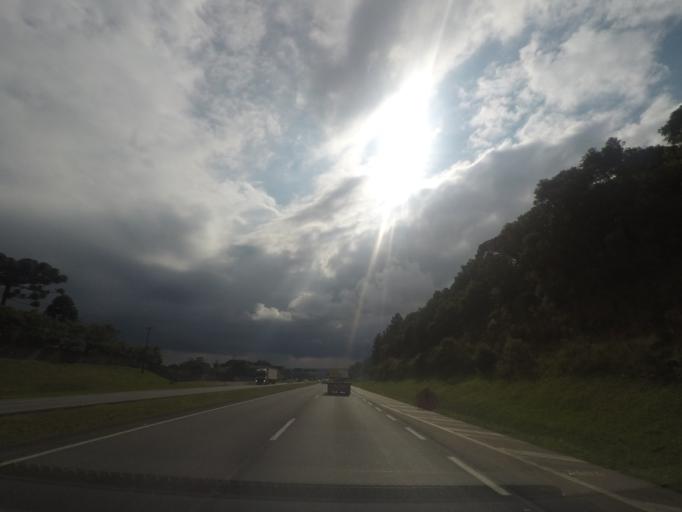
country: BR
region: Parana
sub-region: Sao Jose Dos Pinhais
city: Sao Jose dos Pinhais
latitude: -25.5050
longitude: -49.1424
